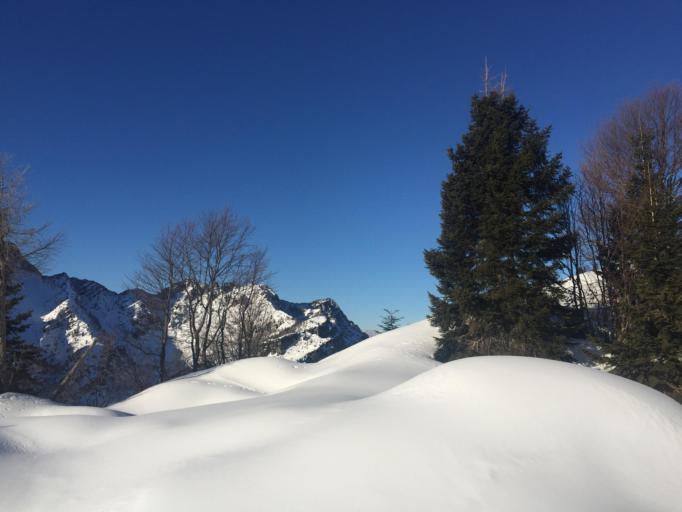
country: IT
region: Friuli Venezia Giulia
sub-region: Provincia di Udine
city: Paularo
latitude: 46.4840
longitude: 13.1552
